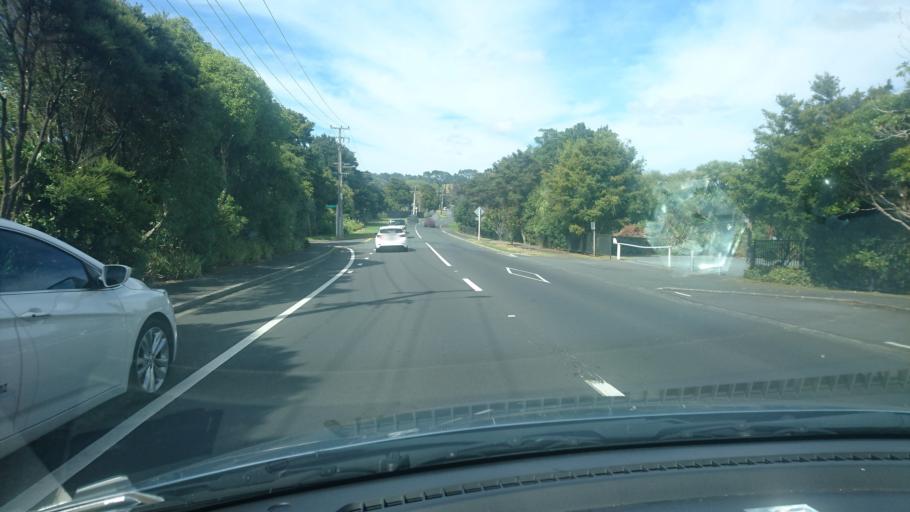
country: NZ
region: Auckland
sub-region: Auckland
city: Muriwai Beach
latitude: -36.7708
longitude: 174.4913
